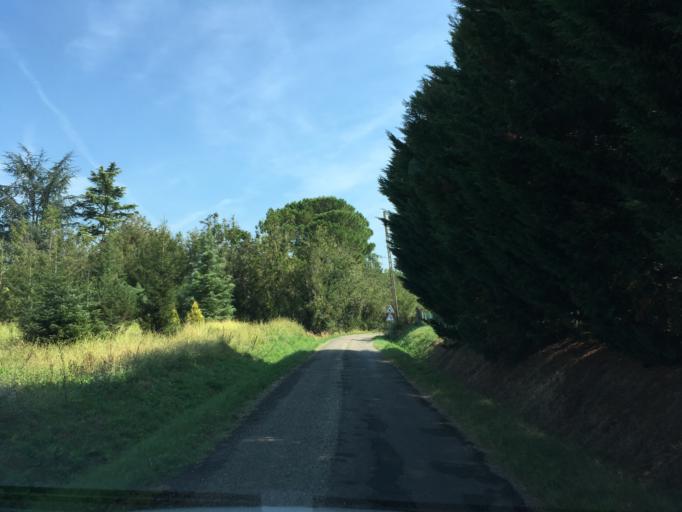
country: FR
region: Midi-Pyrenees
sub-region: Departement du Tarn-et-Garonne
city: Albias
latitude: 44.0614
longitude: 1.4197
